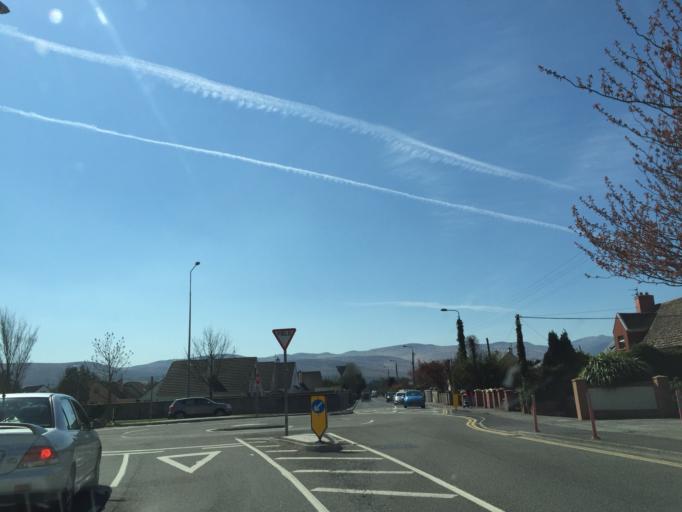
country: IE
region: Munster
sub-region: Ciarrai
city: Tralee
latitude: 52.2638
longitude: -9.6817
